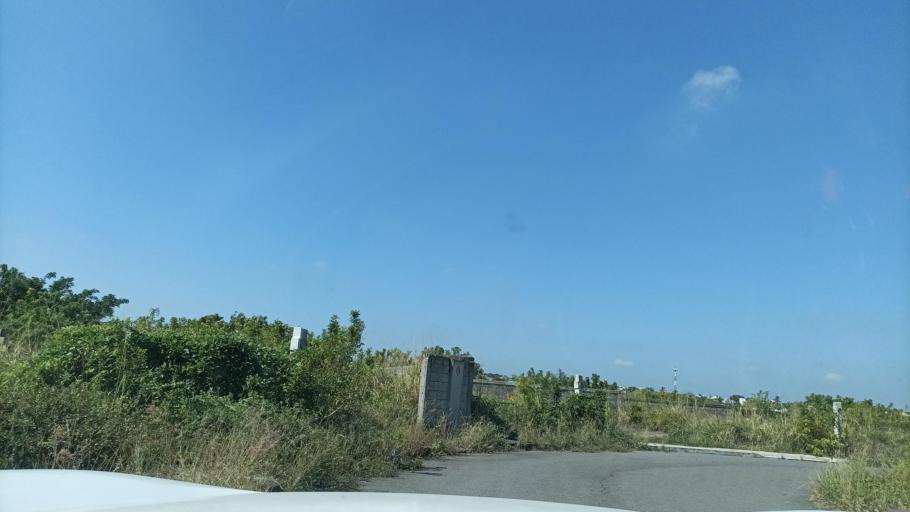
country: MX
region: Veracruz
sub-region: Veracruz
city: Rio Medio [Granja]
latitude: 19.1993
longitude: -96.1791
